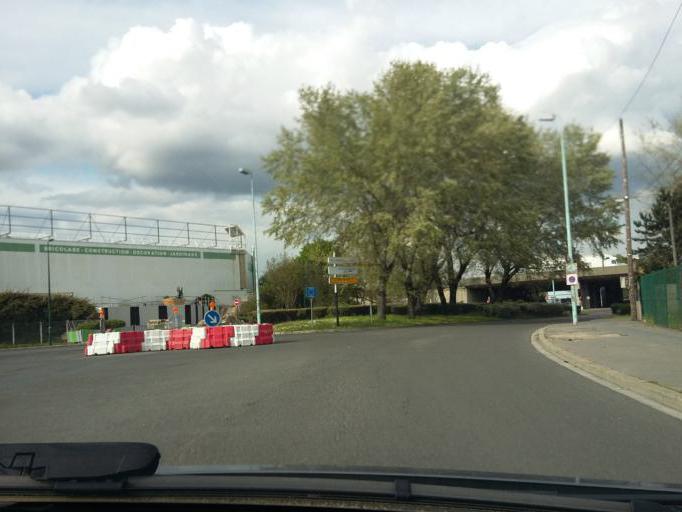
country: FR
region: Ile-de-France
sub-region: Departement des Hauts-de-Seine
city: Villeneuve-la-Garenne
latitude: 48.9309
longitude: 2.3209
